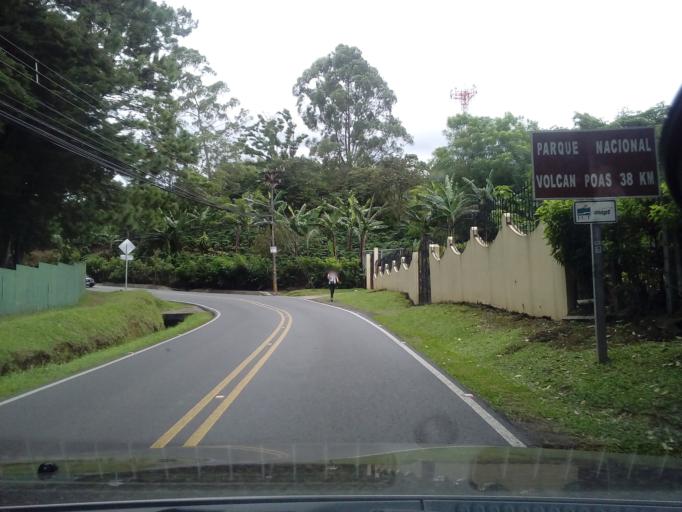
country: CR
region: Heredia
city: Santo Domingo
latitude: 10.0573
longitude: -84.1380
